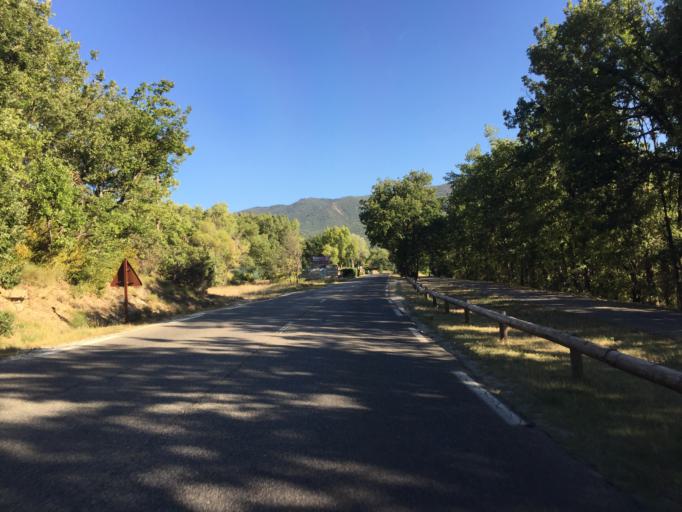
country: FR
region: Provence-Alpes-Cote d'Azur
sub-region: Departement du Vaucluse
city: Saignon
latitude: 43.8580
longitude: 5.4752
